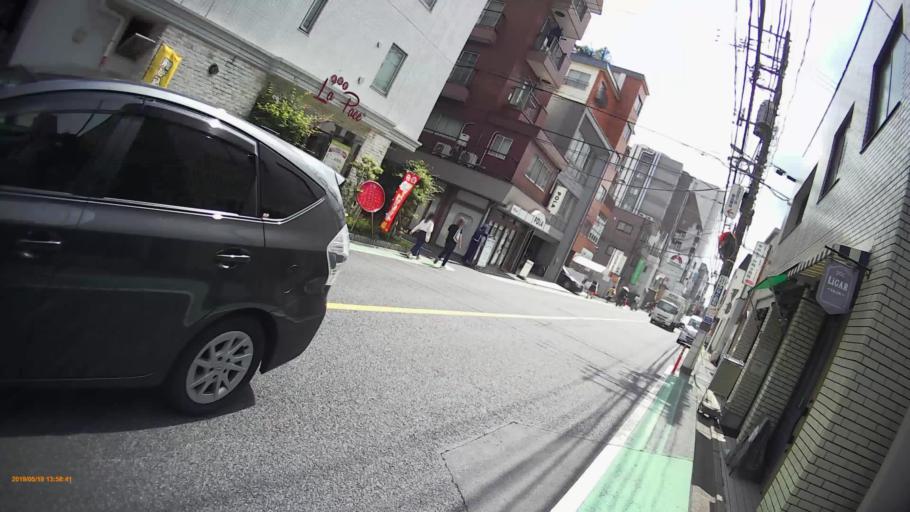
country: JP
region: Tokyo
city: Mitaka-shi
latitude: 35.6694
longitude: 139.6020
